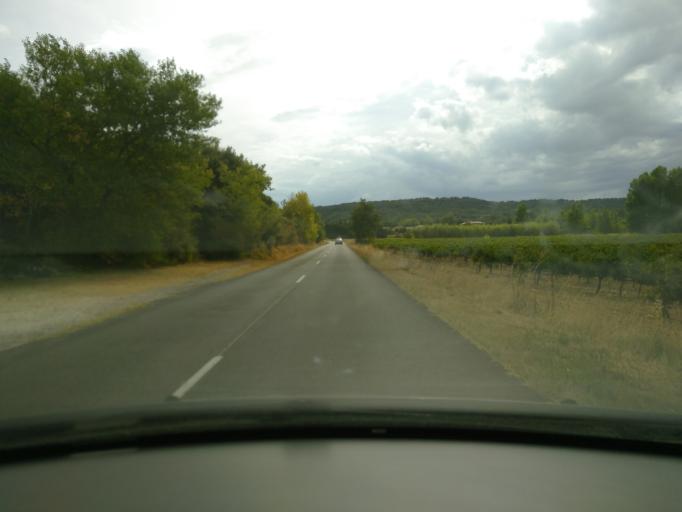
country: FR
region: Rhone-Alpes
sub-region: Departement de la Drome
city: Taulignan
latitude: 44.4333
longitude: 5.0234
